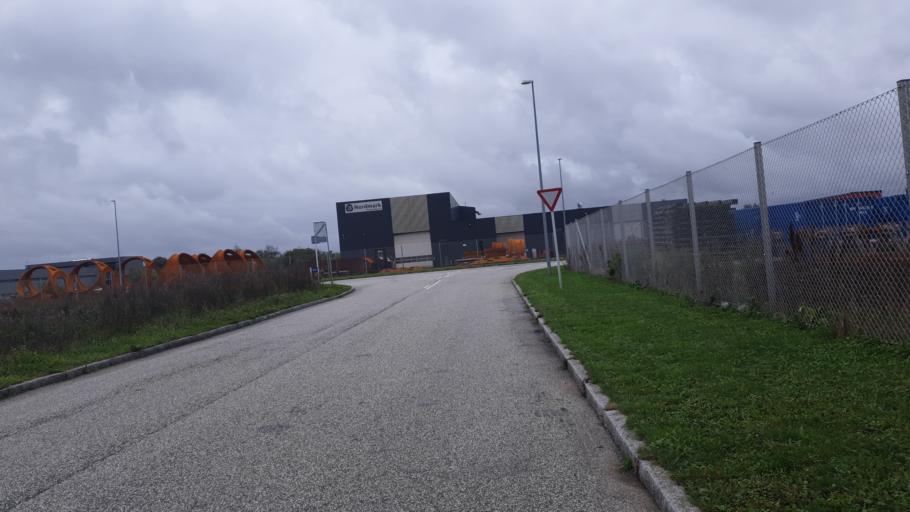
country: DK
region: Central Jutland
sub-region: Hedensted Kommune
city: Hedensted
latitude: 55.7904
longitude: 9.6793
